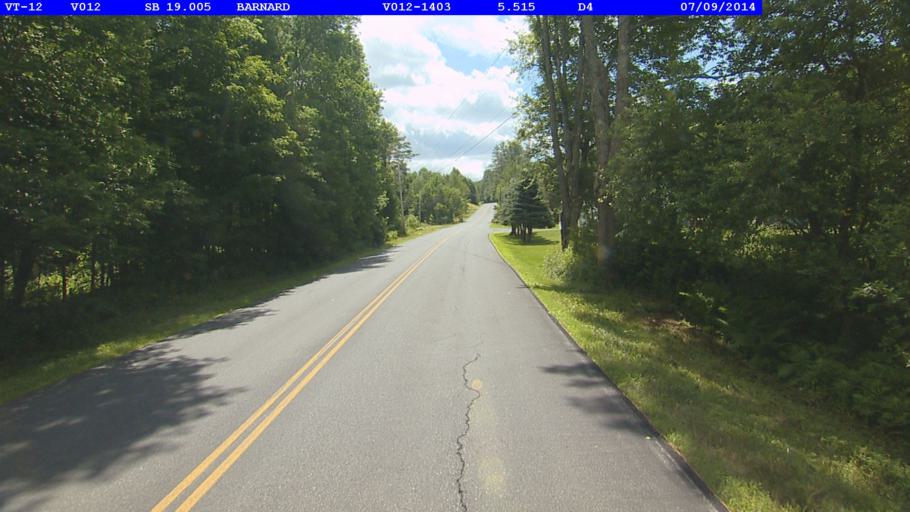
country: US
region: Vermont
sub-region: Windsor County
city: Woodstock
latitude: 43.7371
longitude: -72.6282
